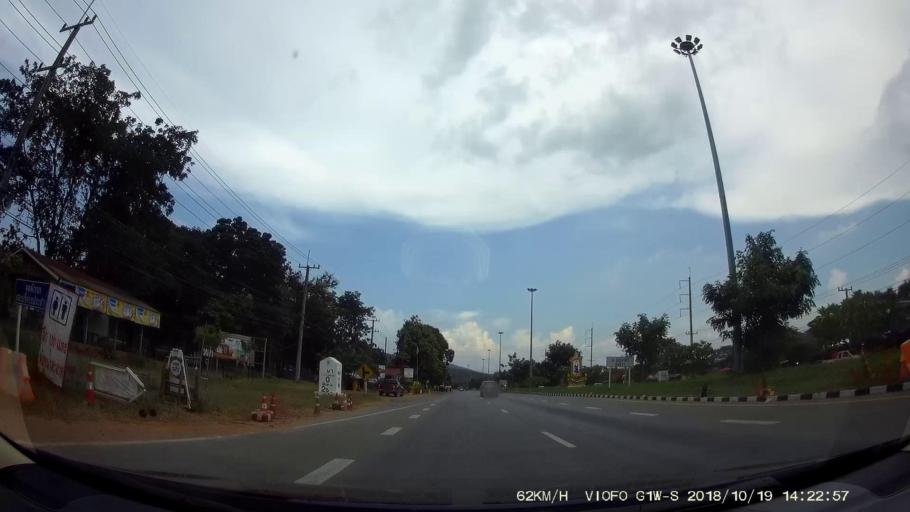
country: TH
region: Chaiyaphum
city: Kaeng Khro
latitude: 16.0672
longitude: 102.2783
